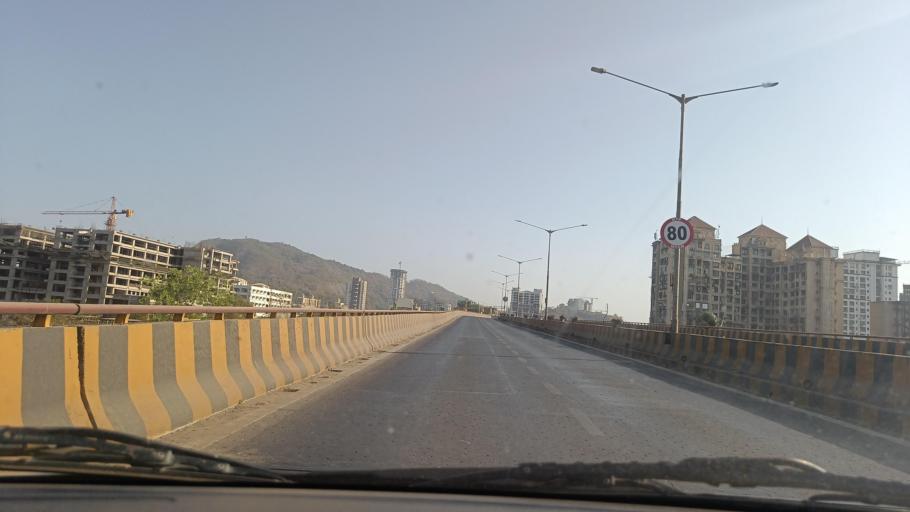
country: IN
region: Maharashtra
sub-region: Mumbai Suburban
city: Mumbai
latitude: 19.0517
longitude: 72.9106
